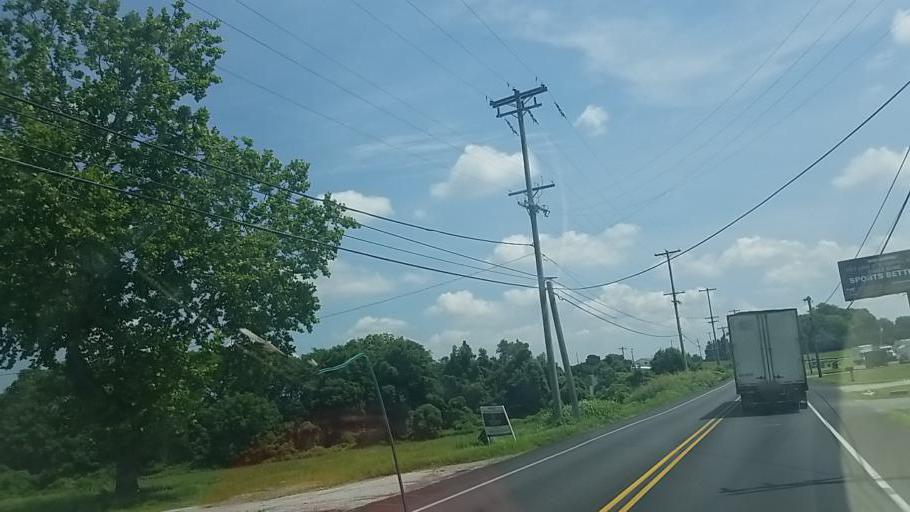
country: US
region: Pennsylvania
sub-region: Chester County
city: Toughkenamon
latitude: 39.8038
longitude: -75.7419
